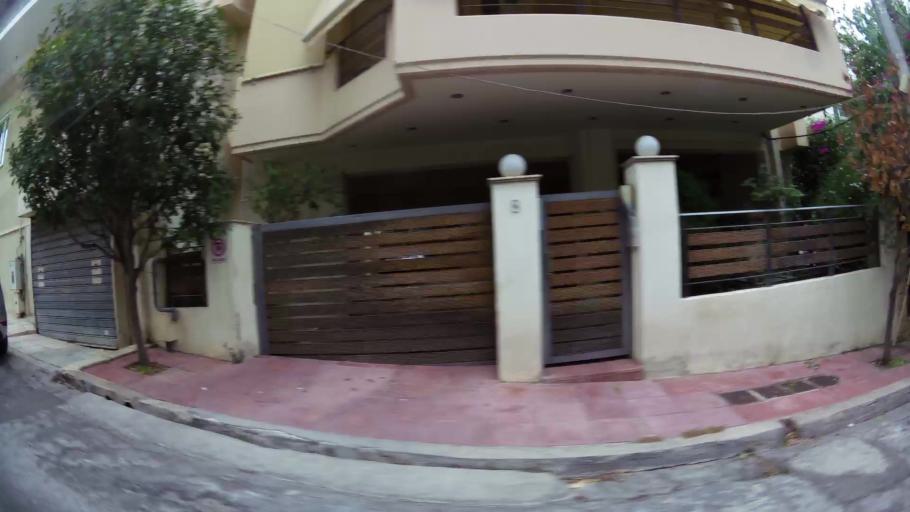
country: GR
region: Attica
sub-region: Nomarchia Athinas
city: Chaidari
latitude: 38.0004
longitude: 23.6685
